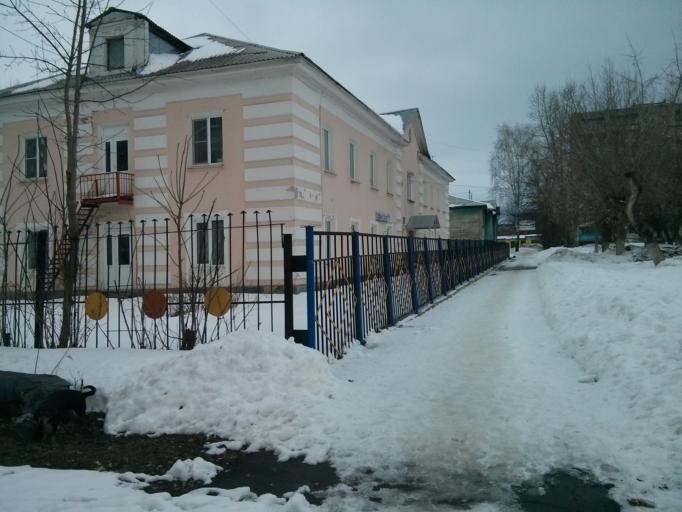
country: RU
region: Vladimir
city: Murom
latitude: 55.5665
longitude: 42.0541
